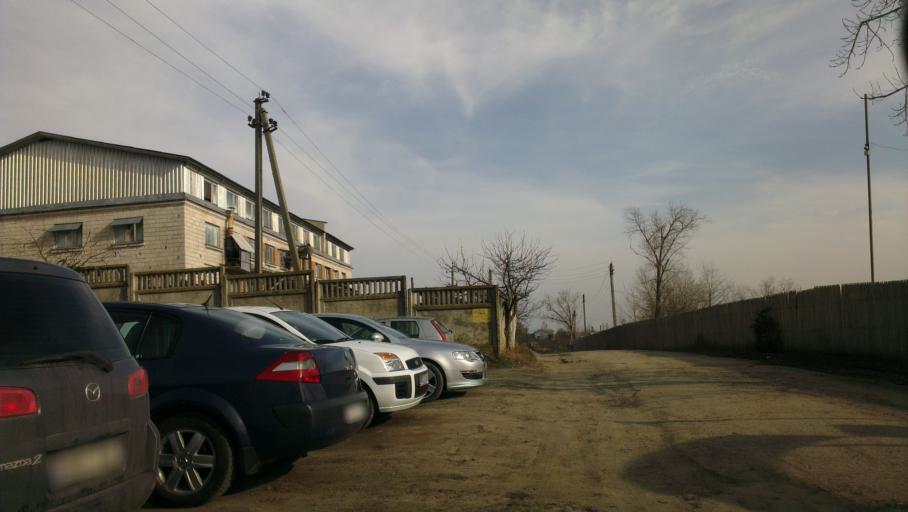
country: MD
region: Laloveni
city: Ialoveni
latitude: 46.9131
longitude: 28.7020
